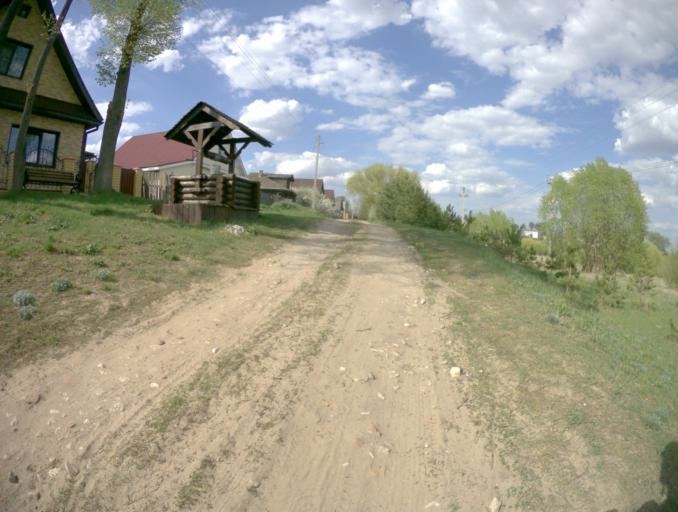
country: RU
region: Vladimir
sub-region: Kovrovskiy Rayon
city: Kovrov
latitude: 56.4420
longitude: 41.3256
